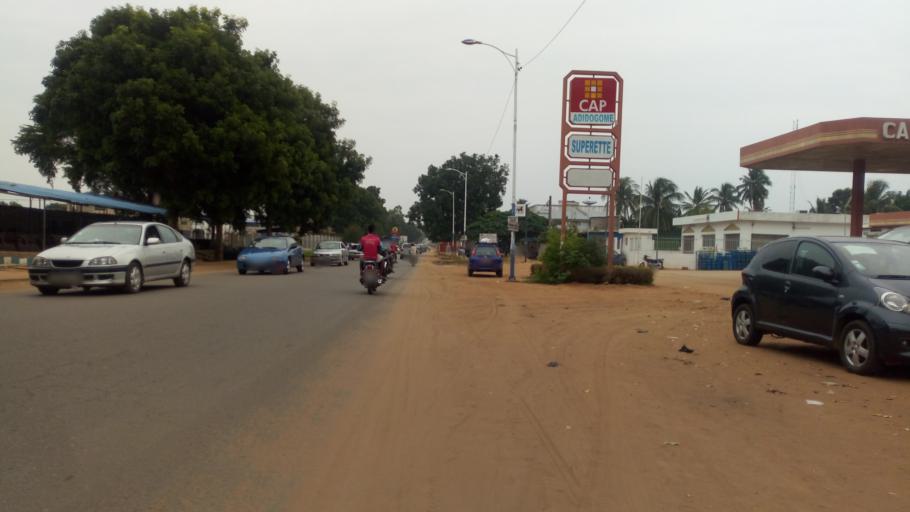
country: TG
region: Maritime
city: Lome
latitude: 6.1777
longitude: 1.1772
